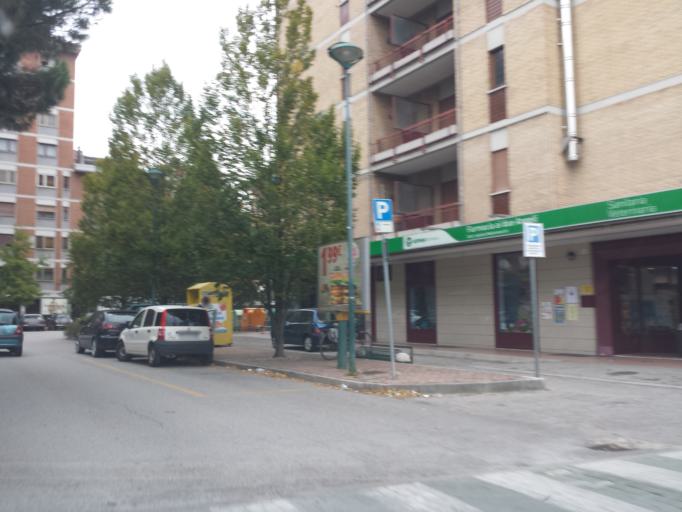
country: IT
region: Veneto
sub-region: Provincia di Venezia
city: Mestre
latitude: 45.4800
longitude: 12.2240
